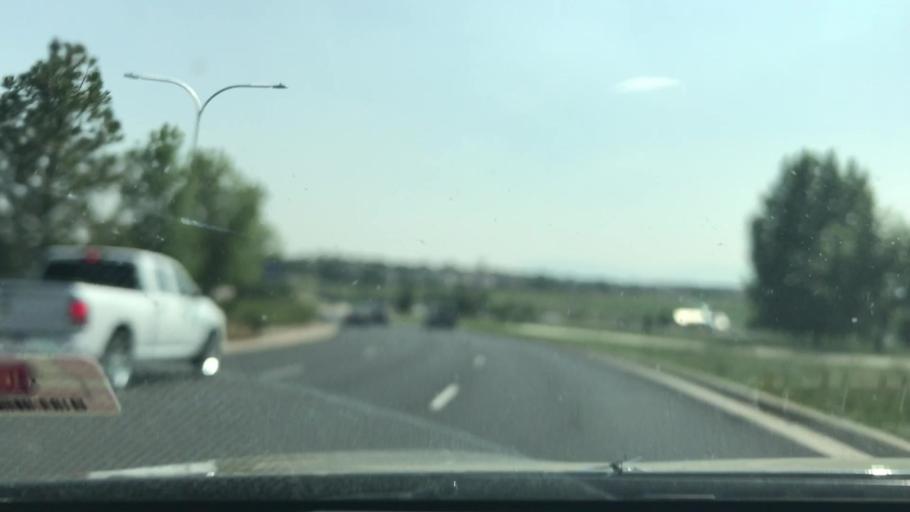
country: US
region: Colorado
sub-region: El Paso County
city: Black Forest
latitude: 38.9678
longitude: -104.7576
